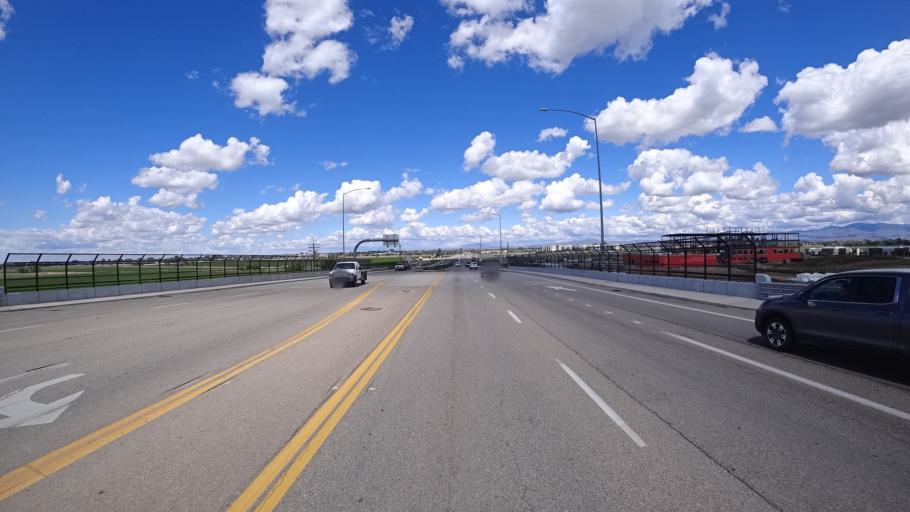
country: US
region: Idaho
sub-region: Ada County
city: Meridian
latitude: 43.5948
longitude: -116.4338
